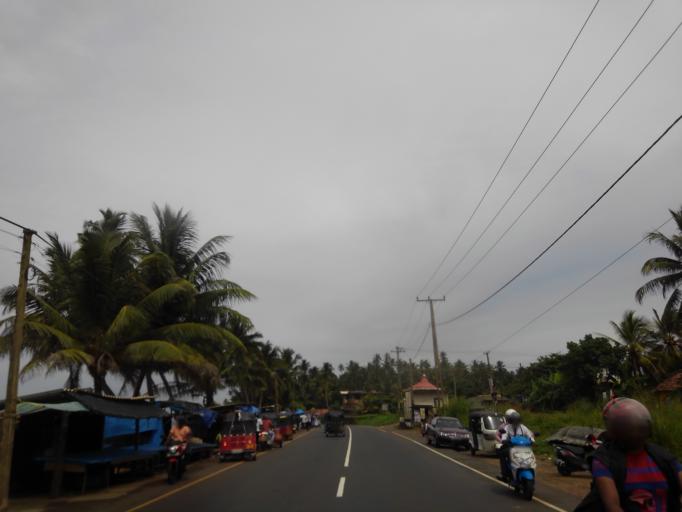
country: LK
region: Western
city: Beruwala
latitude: 6.4870
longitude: 79.9832
